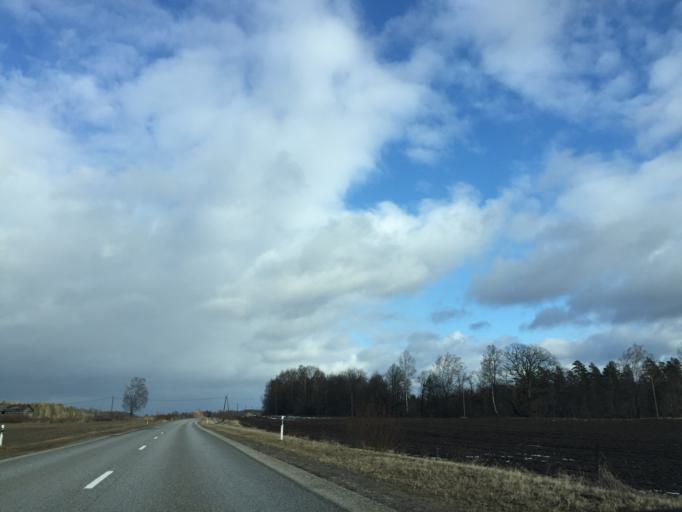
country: LV
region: Aloja
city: Staicele
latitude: 57.8760
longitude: 24.5831
